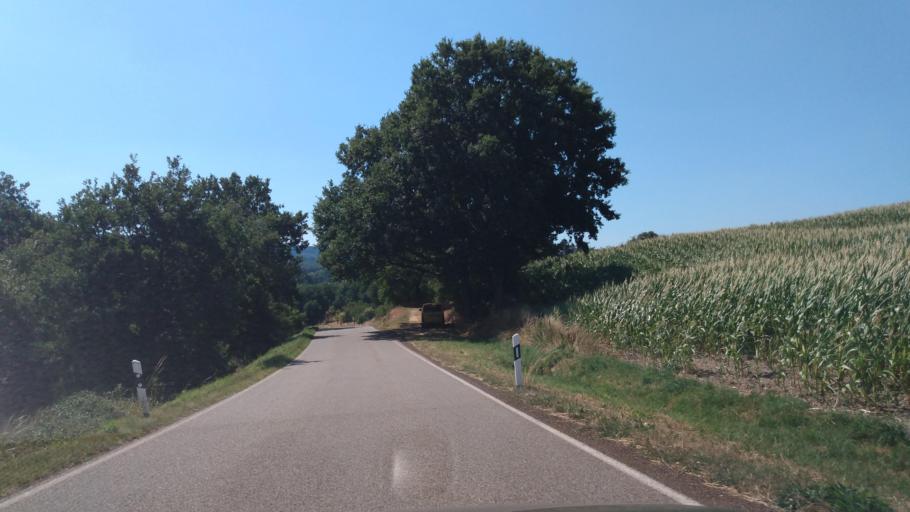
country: DE
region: Rheinland-Pfalz
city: Morbach
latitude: 49.8262
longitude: 7.1504
